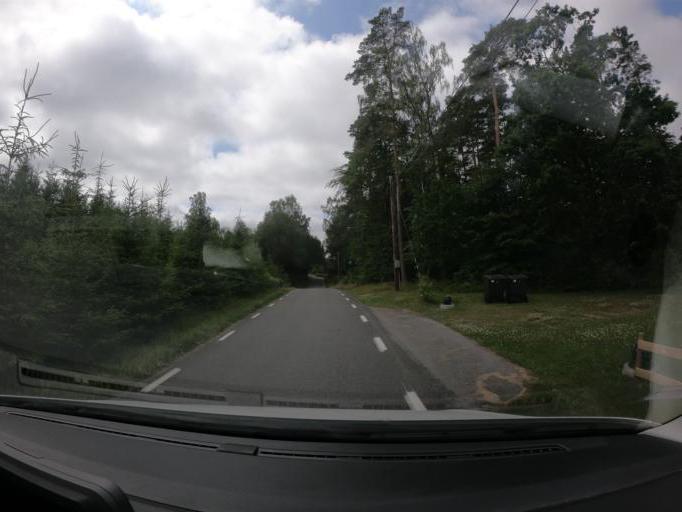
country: SE
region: Skane
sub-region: Hassleholms Kommun
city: Sosdala
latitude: 56.1113
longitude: 13.6144
